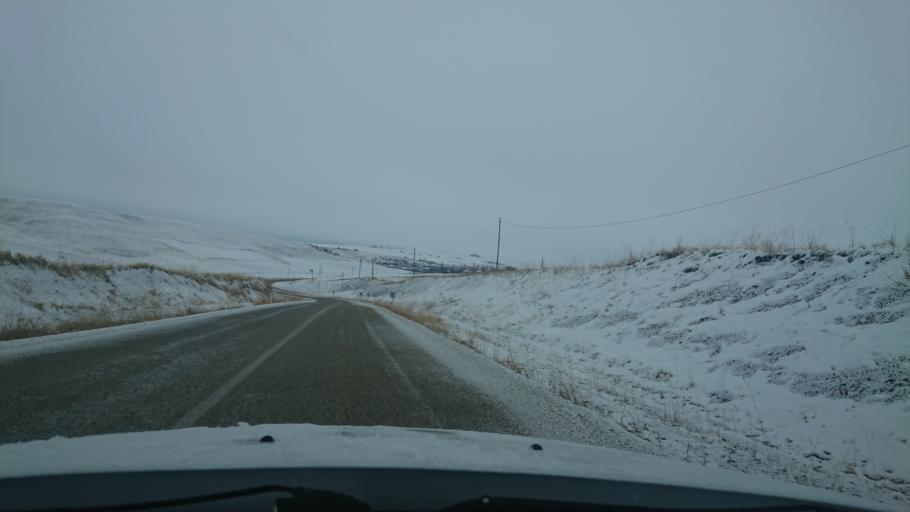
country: TR
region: Aksaray
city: Agacoren
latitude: 38.7937
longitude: 33.8707
